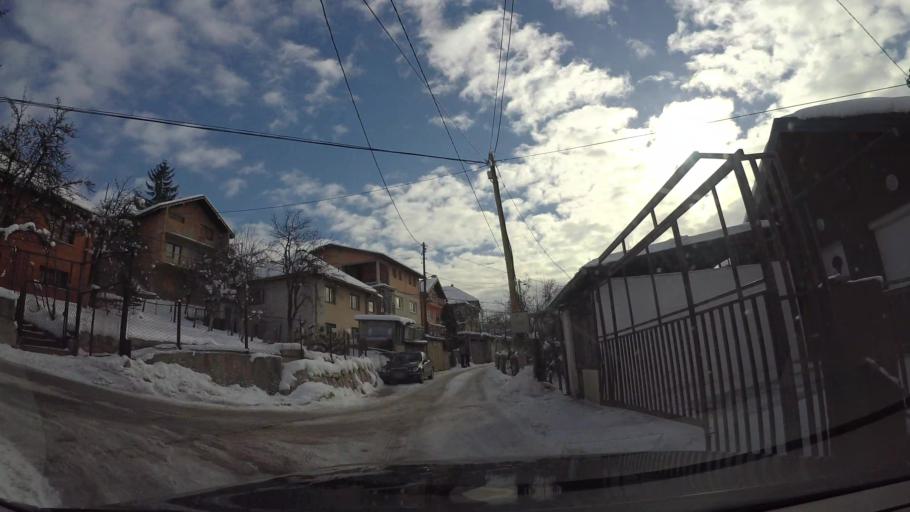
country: BA
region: Federation of Bosnia and Herzegovina
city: Kobilja Glava
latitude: 43.8767
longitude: 18.4176
